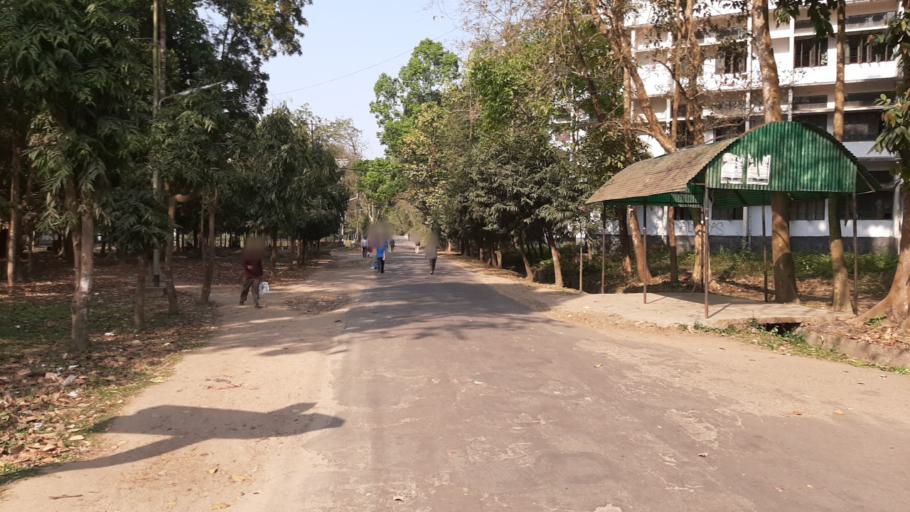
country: BD
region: Chittagong
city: Chittagong
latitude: 22.4718
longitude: 91.7872
